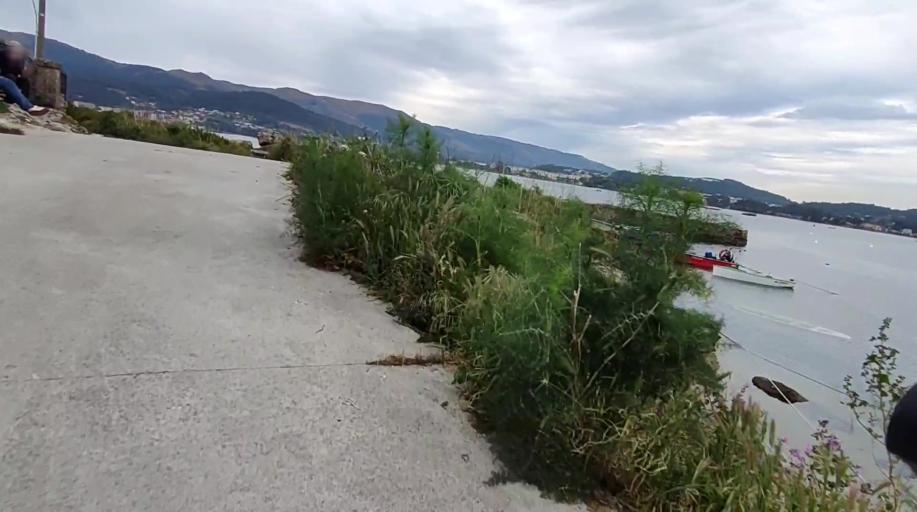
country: ES
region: Galicia
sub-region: Provincia da Coruna
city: Boiro
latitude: 42.6257
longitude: -8.8825
